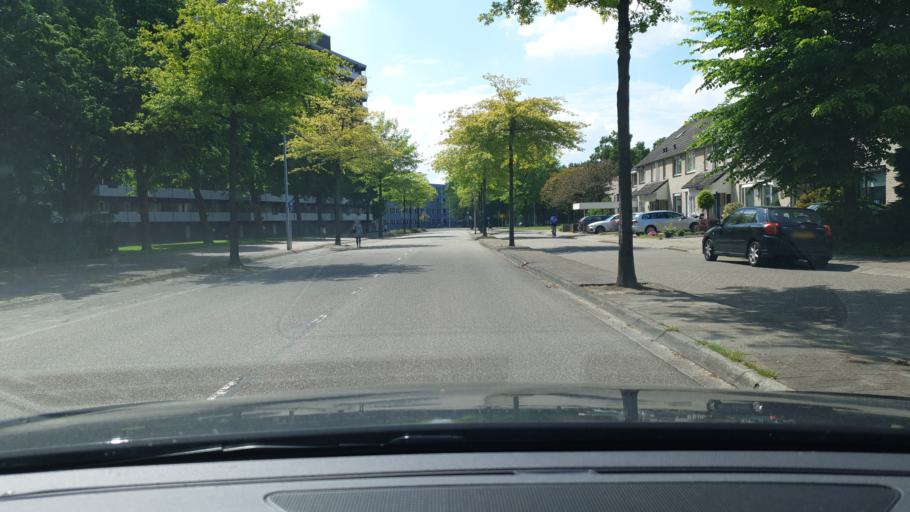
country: NL
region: North Brabant
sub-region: Gemeente Eindhoven
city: Eindhoven
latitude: 51.4370
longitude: 5.4635
